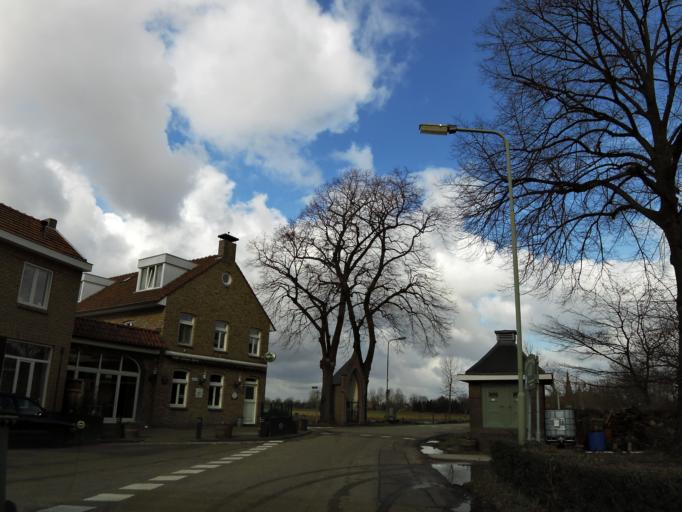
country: NL
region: Limburg
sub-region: Gemeente Meerssen
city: Meerssen
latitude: 50.9239
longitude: 5.7398
